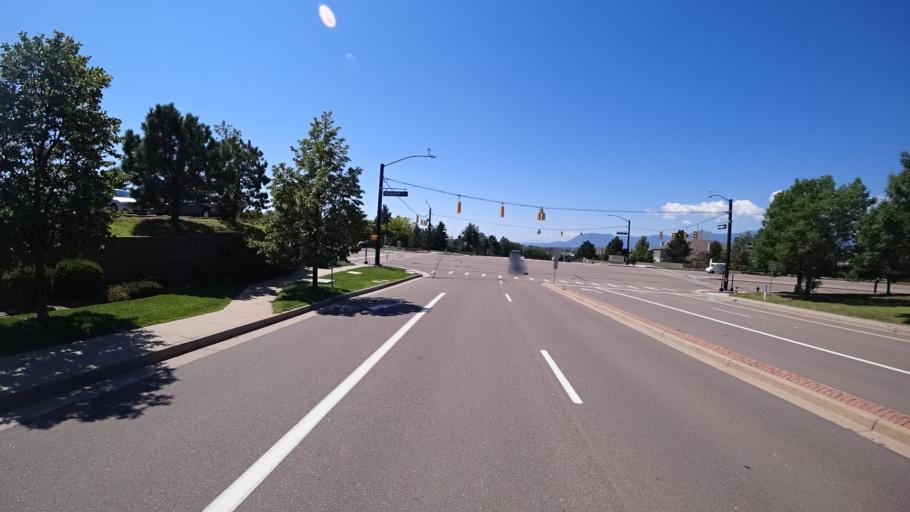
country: US
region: Colorado
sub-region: El Paso County
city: Black Forest
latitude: 38.9575
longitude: -104.7696
